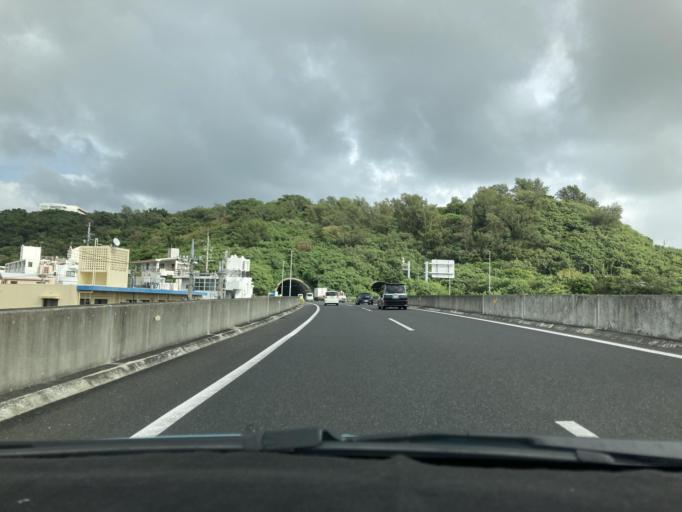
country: JP
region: Okinawa
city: Tomigusuku
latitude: 26.1716
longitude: 127.6786
